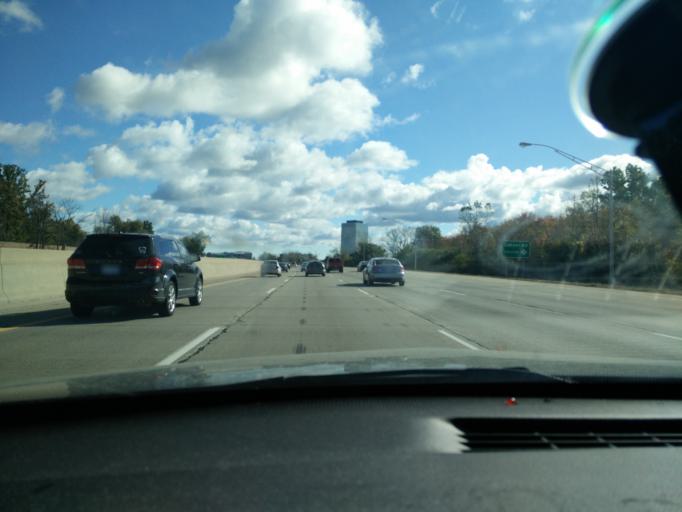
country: US
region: Michigan
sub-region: Oakland County
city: Franklin
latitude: 42.4907
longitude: -83.3138
